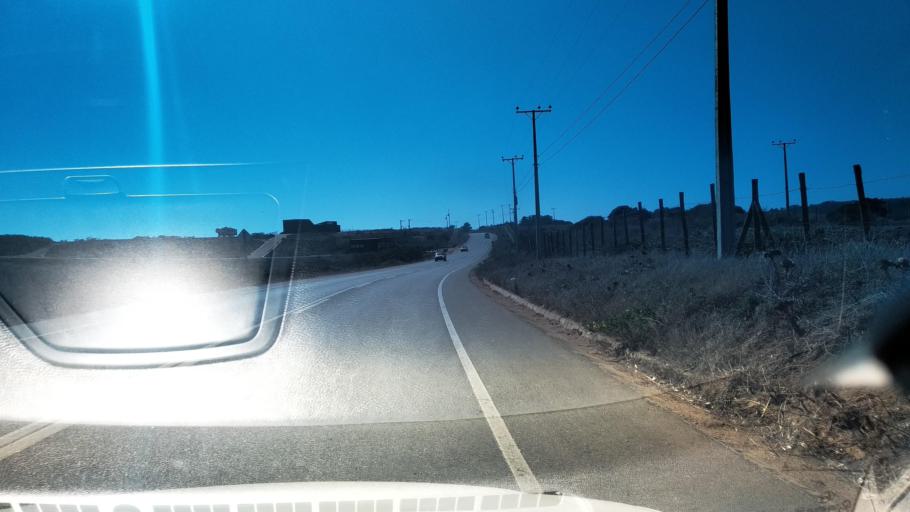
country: CL
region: O'Higgins
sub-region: Provincia de Colchagua
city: Santa Cruz
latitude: -34.4472
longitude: -72.0317
